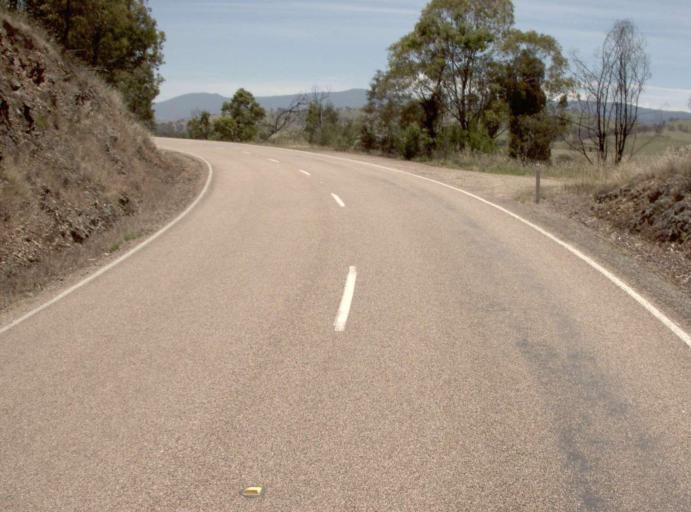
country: AU
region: Victoria
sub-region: East Gippsland
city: Bairnsdale
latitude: -37.4226
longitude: 147.8350
